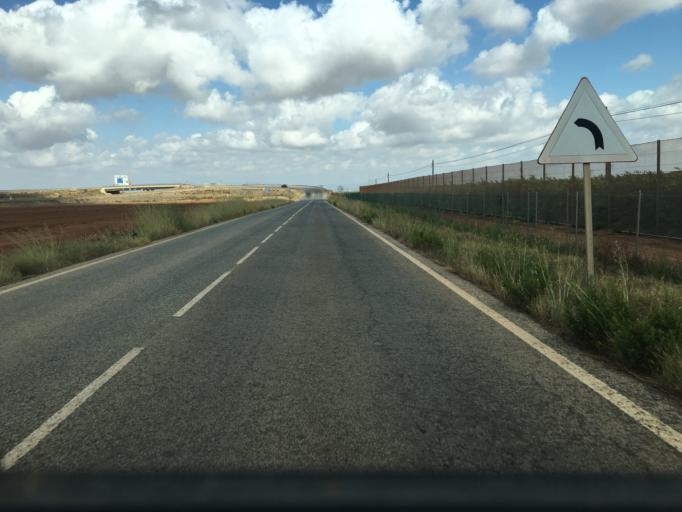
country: ES
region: Murcia
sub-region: Murcia
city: La Union
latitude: 37.6498
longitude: -0.8802
